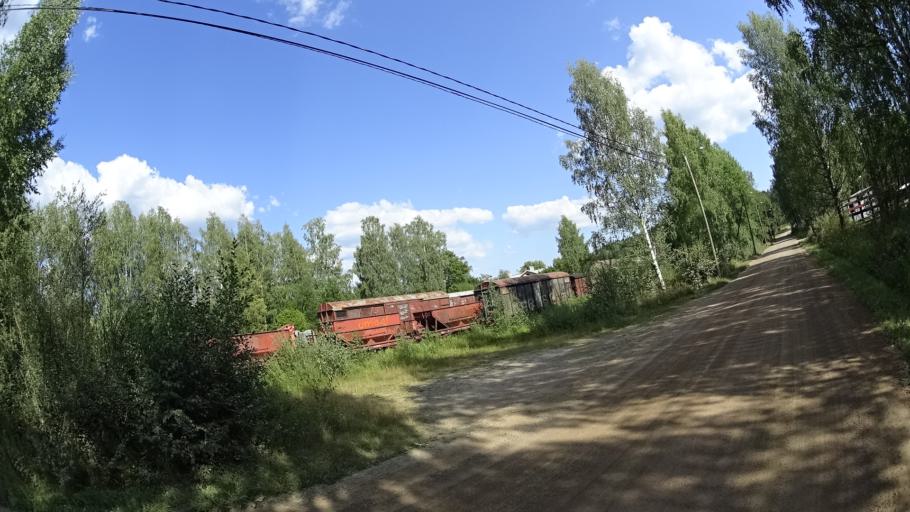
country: FI
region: Uusimaa
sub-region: Porvoo
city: Porvoo
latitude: 60.3973
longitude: 25.6440
